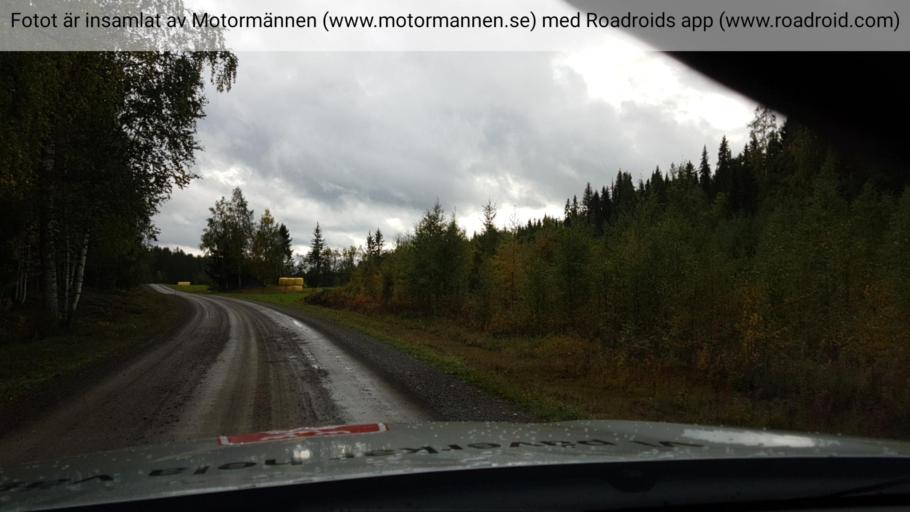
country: SE
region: Norrbotten
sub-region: Alvsbyns Kommun
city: AElvsbyn
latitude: 66.1462
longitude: 20.8631
